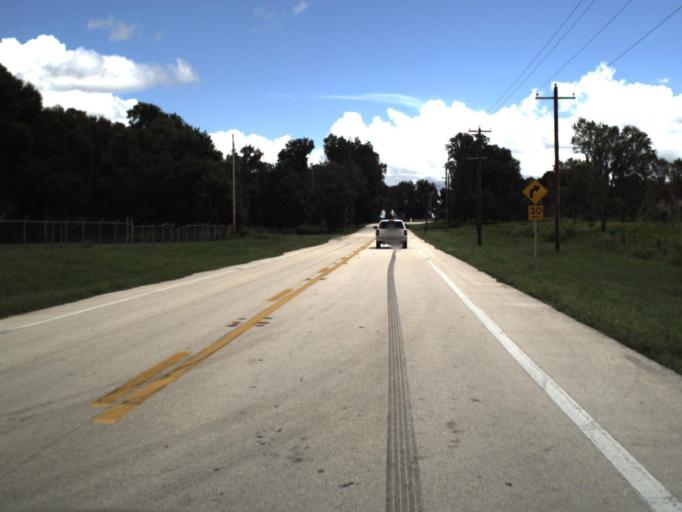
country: US
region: Florida
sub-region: Polk County
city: Fort Meade
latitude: 27.7517
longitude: -81.7688
